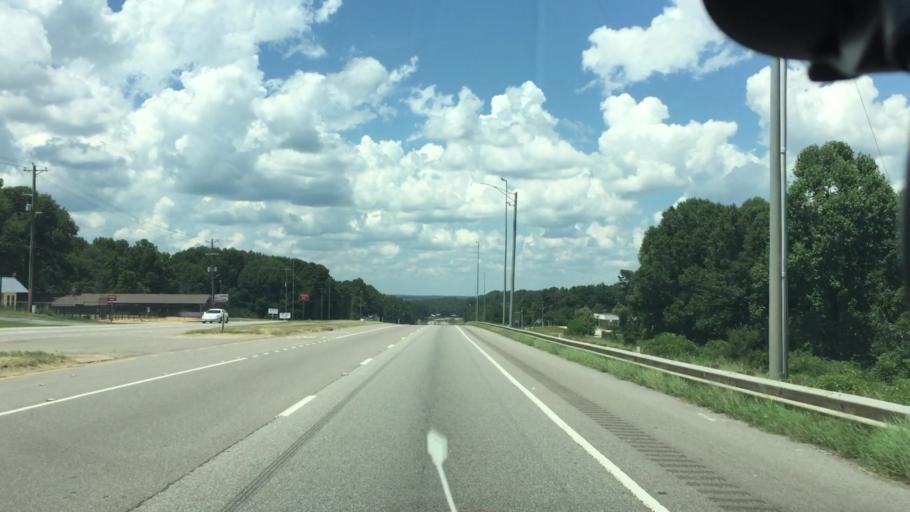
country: US
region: Alabama
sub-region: Pike County
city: Troy
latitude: 31.8097
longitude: -85.9915
